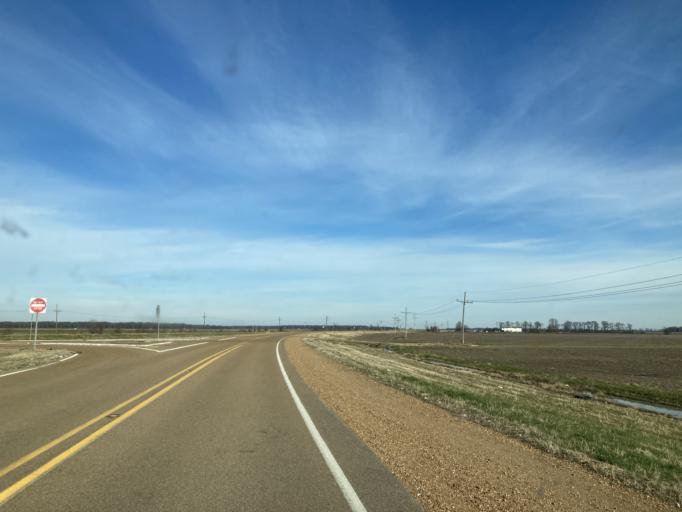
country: US
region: Mississippi
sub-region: Humphreys County
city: Belzoni
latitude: 32.9896
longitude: -90.5885
